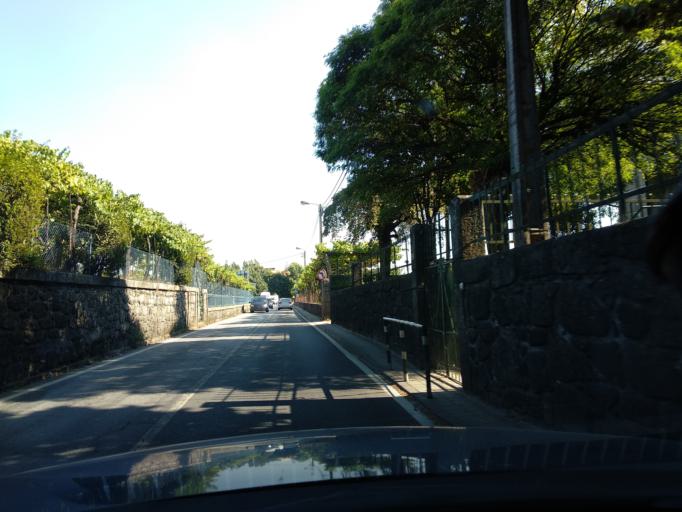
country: PT
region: Porto
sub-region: Paredes
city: Madalena
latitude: 41.2302
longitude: -8.3627
